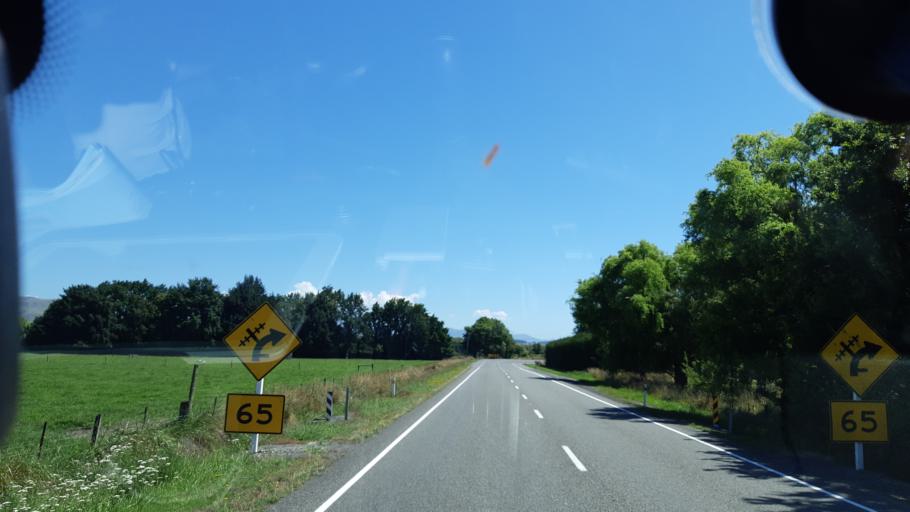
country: NZ
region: Canterbury
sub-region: Kaikoura District
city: Kaikoura
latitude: -42.7417
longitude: 173.2667
